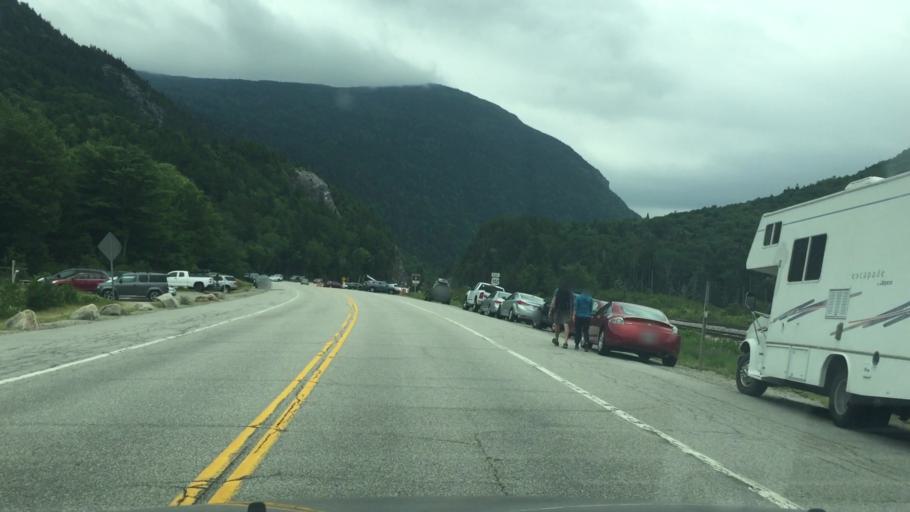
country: US
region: New Hampshire
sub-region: Grafton County
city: Deerfield
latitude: 44.2164
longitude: -71.4098
